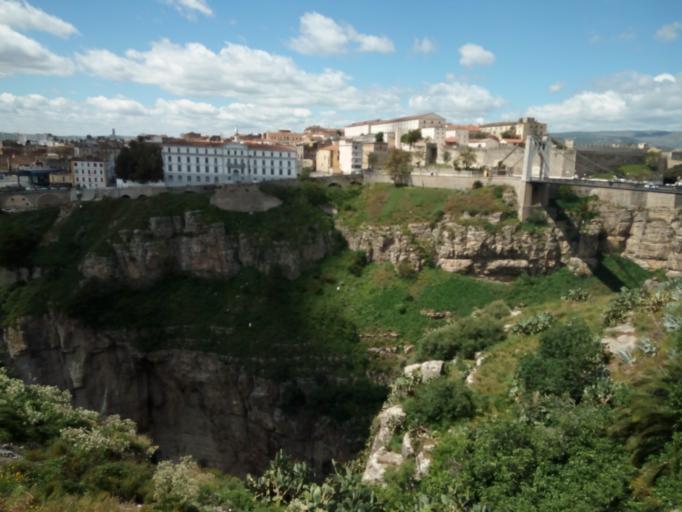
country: DZ
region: Constantine
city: Constantine
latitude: 36.3725
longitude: 6.6164
